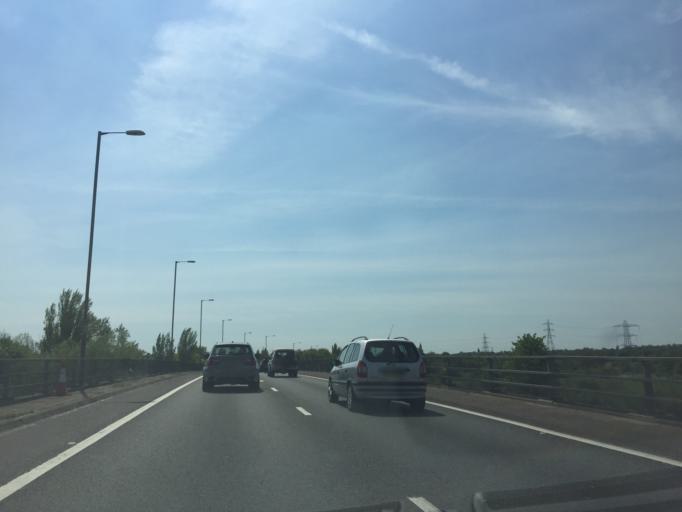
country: GB
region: England
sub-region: Greater London
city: Woodford Green
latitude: 51.6003
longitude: 0.0478
